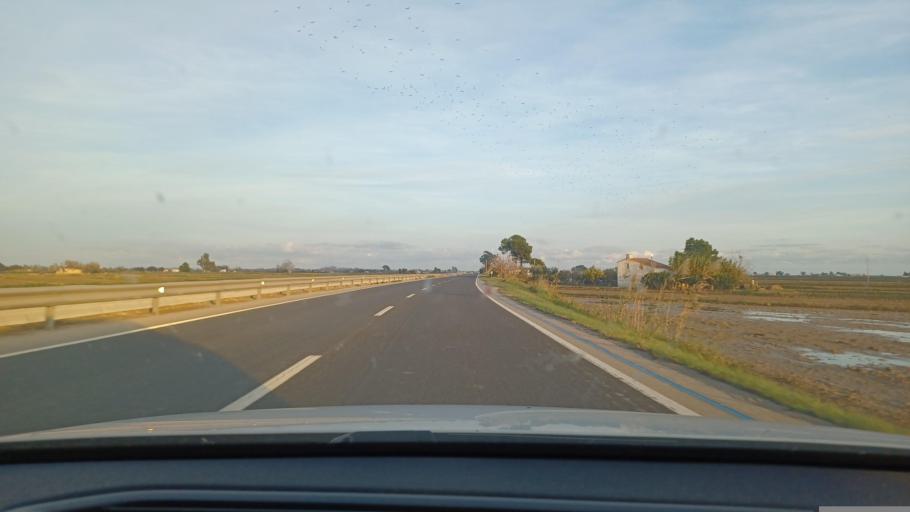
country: ES
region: Catalonia
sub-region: Provincia de Tarragona
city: Deltebre
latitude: 40.7097
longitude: 0.6474
